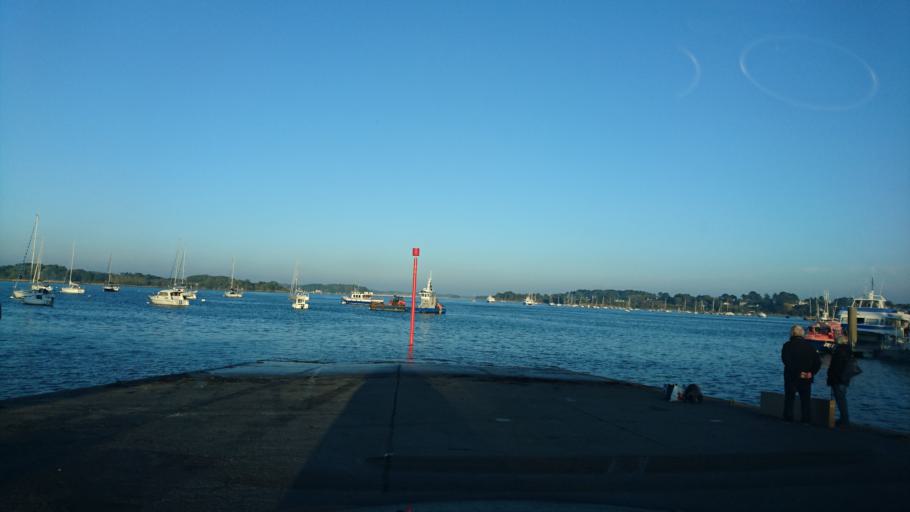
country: FR
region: Brittany
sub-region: Departement du Morbihan
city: Larmor-Baden
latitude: 47.6028
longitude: -2.8603
